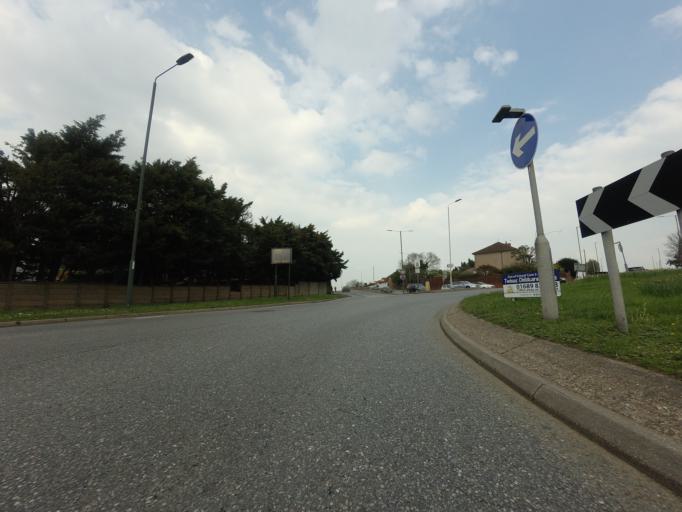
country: GB
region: England
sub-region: Greater London
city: Sidcup
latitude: 51.4153
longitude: 0.1264
